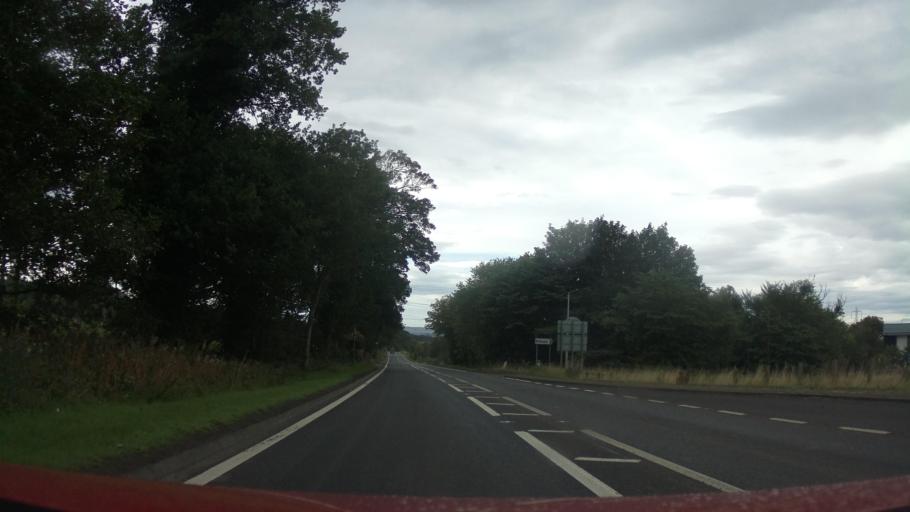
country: GB
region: Scotland
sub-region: Fife
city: Kincardine
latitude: 56.0925
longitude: -3.7185
